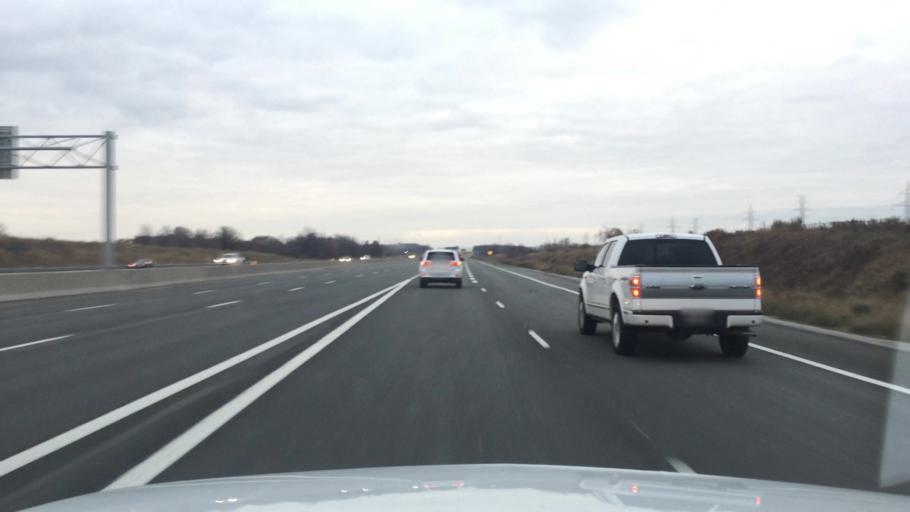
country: CA
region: Ontario
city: Oakville
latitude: 43.5202
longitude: -79.7348
